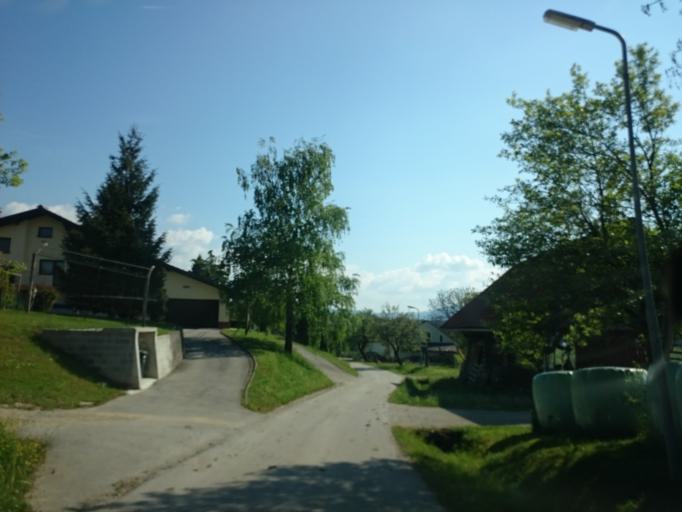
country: SI
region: Sentjur pri Celju
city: Sentjur
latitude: 46.2678
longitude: 15.3869
